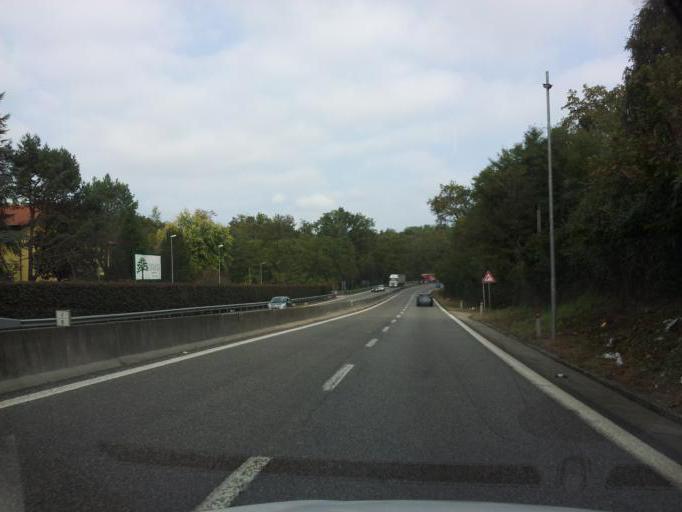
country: IT
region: Lombardy
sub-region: Provincia di Varese
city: Vergiate
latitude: 45.7239
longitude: 8.6782
